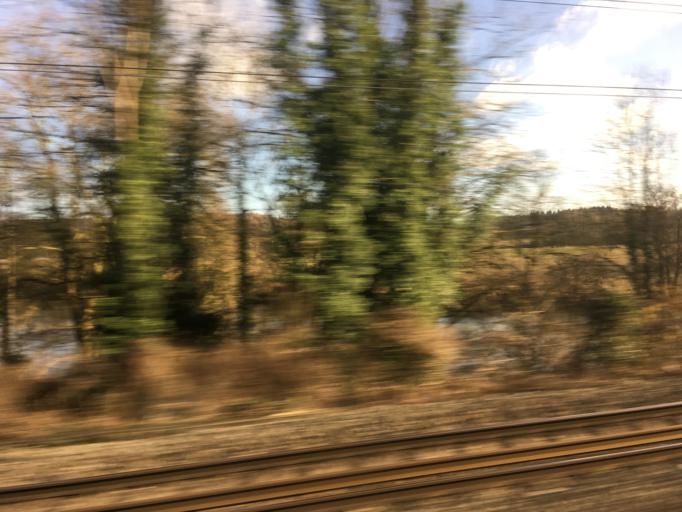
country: GB
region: England
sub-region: West Berkshire
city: Tilehurst
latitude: 51.4770
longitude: -1.0400
